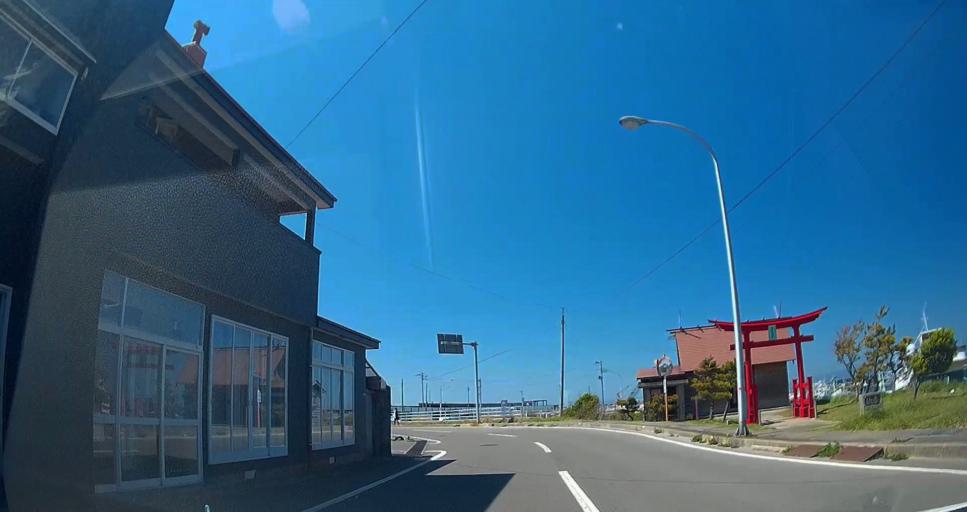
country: JP
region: Hokkaido
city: Hakodate
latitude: 41.5242
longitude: 140.9006
